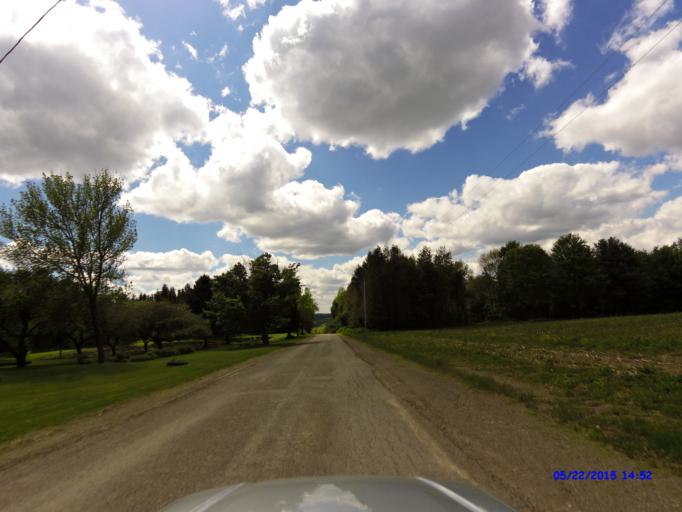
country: US
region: New York
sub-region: Cattaraugus County
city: Franklinville
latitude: 42.3818
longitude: -78.5752
